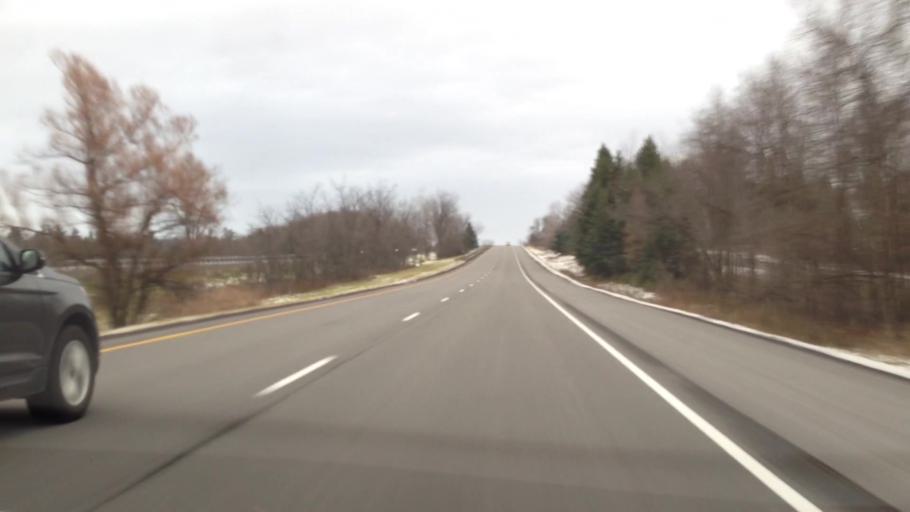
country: CA
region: Quebec
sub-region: Monteregie
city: Rigaud
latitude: 45.5424
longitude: -74.4043
